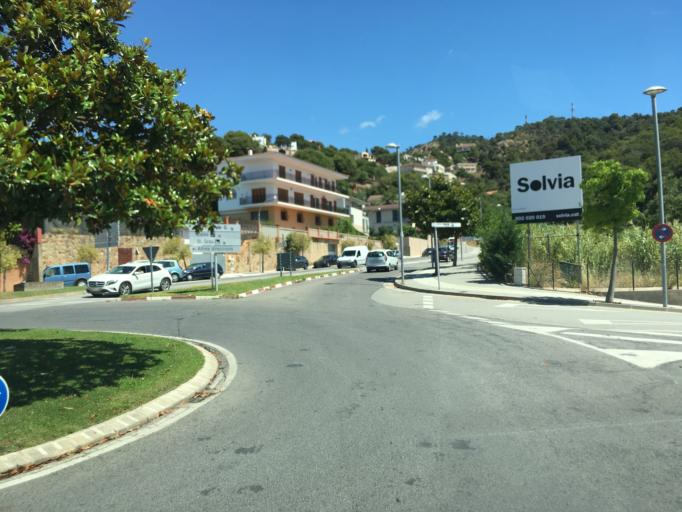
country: ES
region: Catalonia
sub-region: Provincia de Girona
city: Tossa de Mar
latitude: 41.7248
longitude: 2.9329
